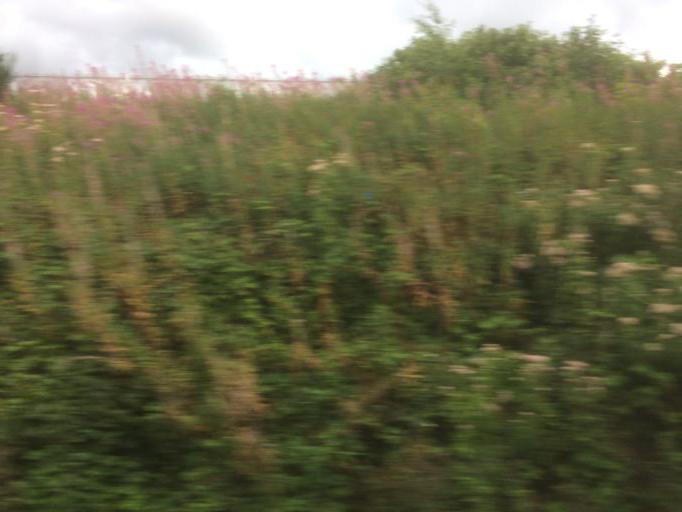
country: GB
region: Scotland
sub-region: Glasgow City
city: Glasgow
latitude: 55.8750
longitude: -4.2430
